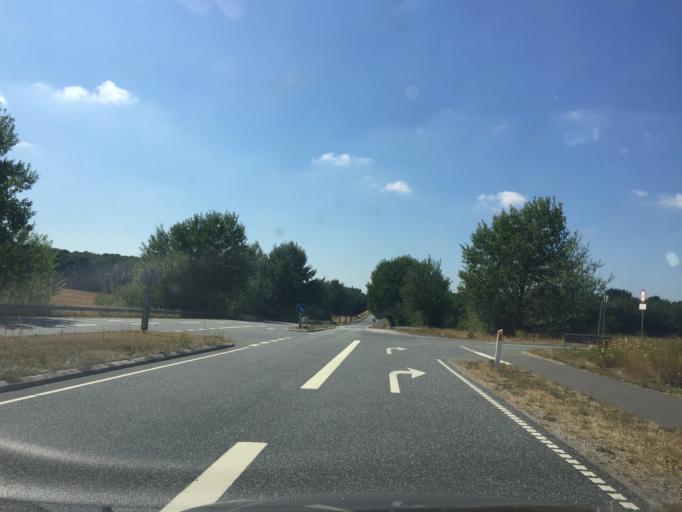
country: DK
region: Capital Region
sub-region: Allerod Kommune
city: Lynge
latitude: 55.8352
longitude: 12.2554
